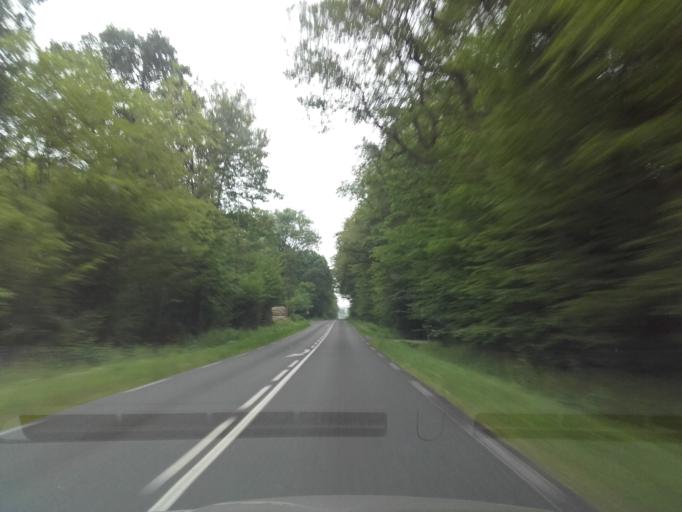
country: FR
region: Centre
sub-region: Departement d'Indre-et-Loire
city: Cerelles
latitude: 47.5035
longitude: 0.6968
